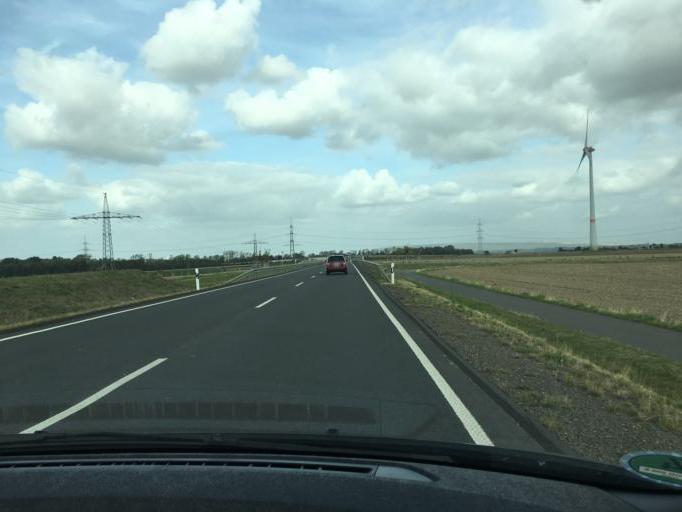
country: DE
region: North Rhine-Westphalia
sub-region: Regierungsbezirk Koln
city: Langerwehe
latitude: 50.8269
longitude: 6.3806
